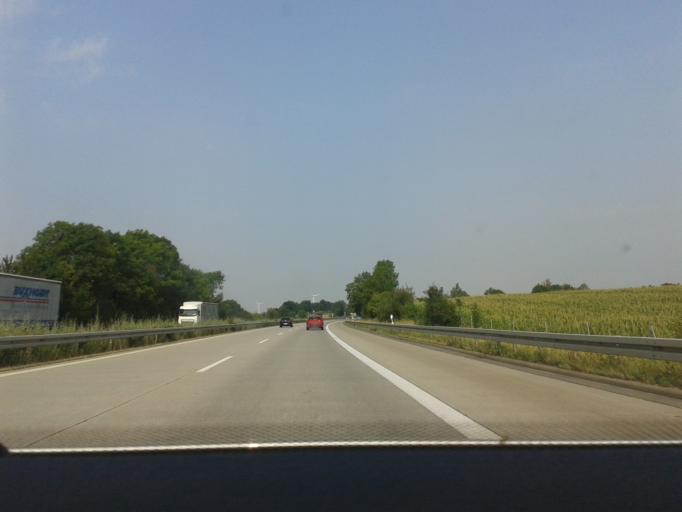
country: DE
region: Saxony
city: Grossweitzschen
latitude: 51.1703
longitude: 13.0451
